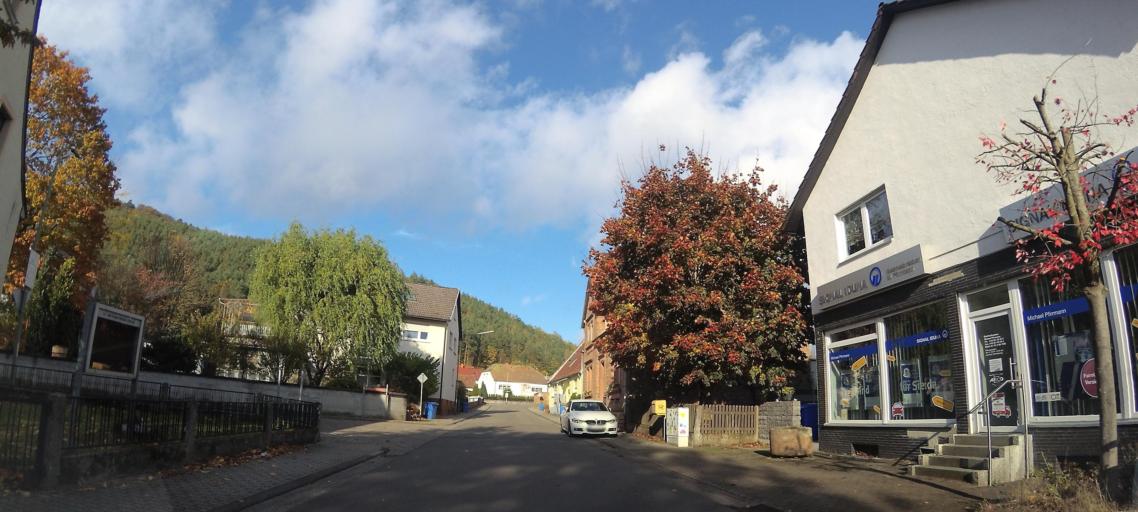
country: DE
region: Rheinland-Pfalz
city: Ruppertsweiler
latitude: 49.1973
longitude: 7.6856
